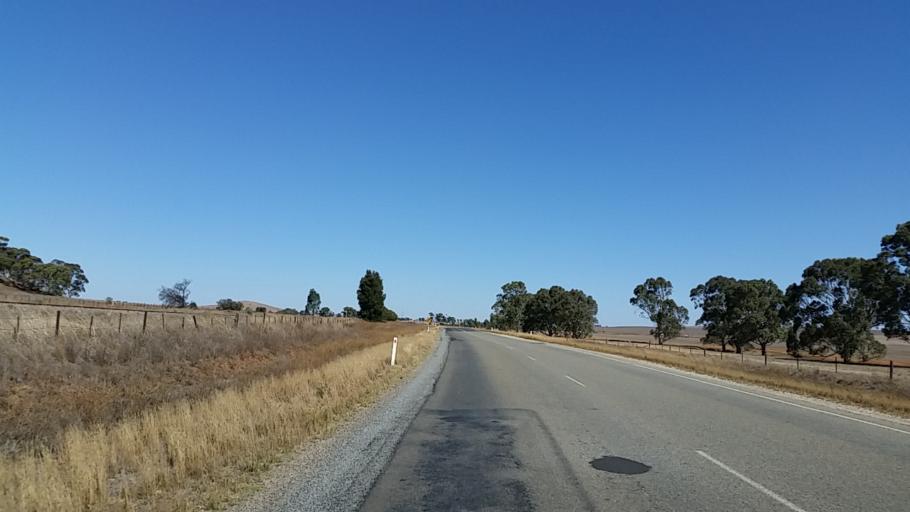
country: AU
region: South Australia
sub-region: Clare and Gilbert Valleys
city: Clare
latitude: -33.6787
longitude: 138.9135
